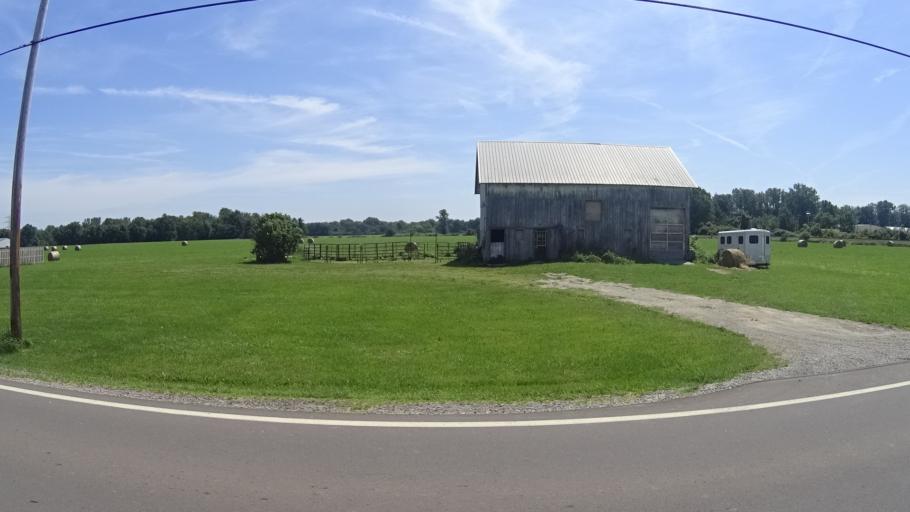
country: US
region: Ohio
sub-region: Erie County
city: Huron
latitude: 41.3546
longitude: -82.4941
